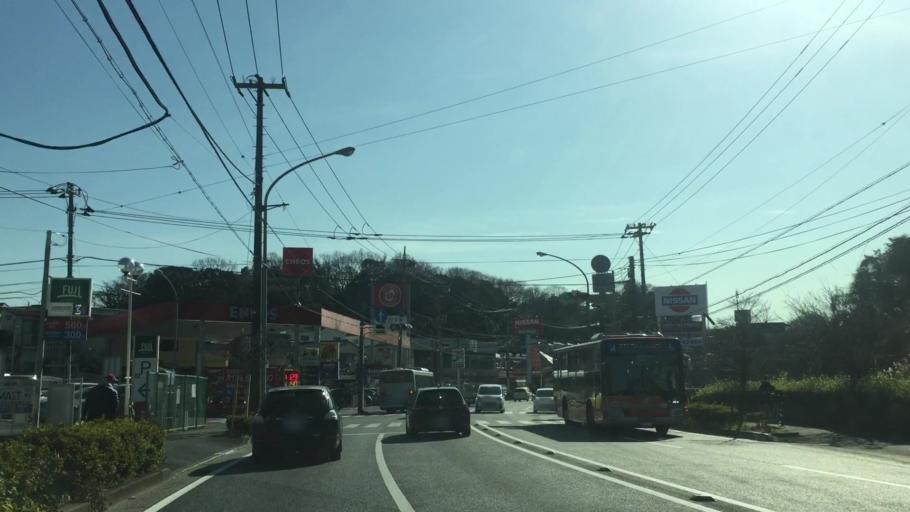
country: JP
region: Kanagawa
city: Zushi
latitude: 35.3688
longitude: 139.6134
